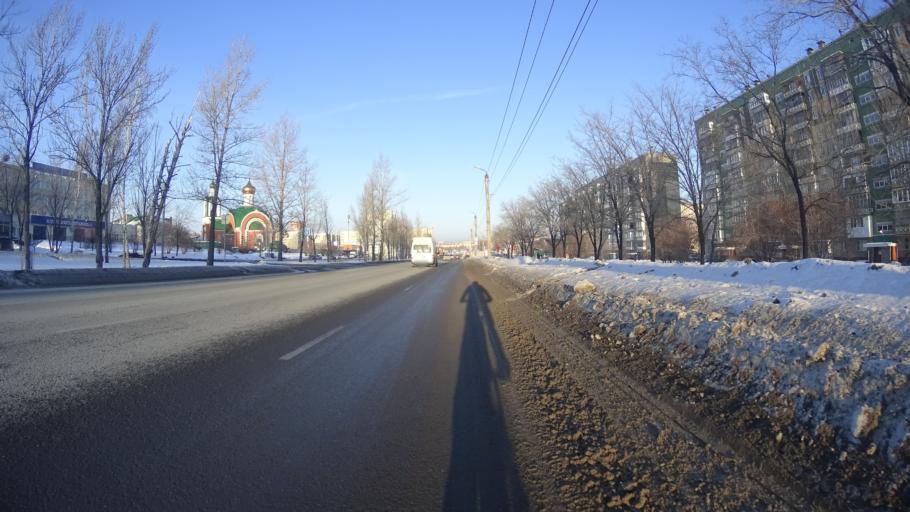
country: RU
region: Chelyabinsk
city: Roshchino
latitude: 55.1805
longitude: 61.2876
